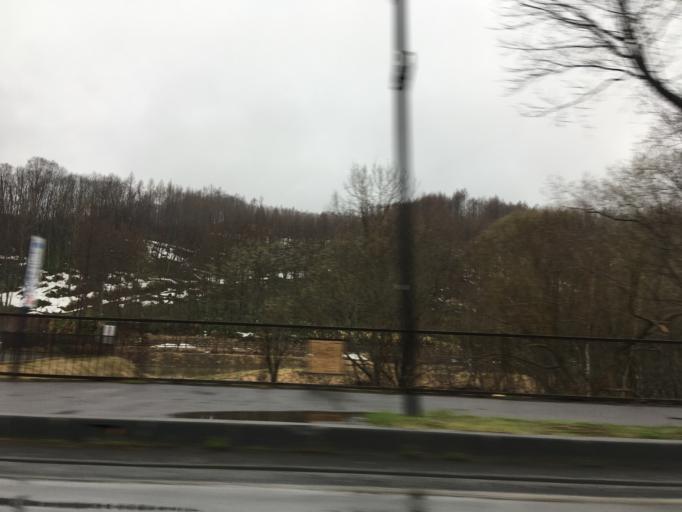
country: JP
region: Hokkaido
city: Nayoro
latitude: 44.0909
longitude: 142.4398
